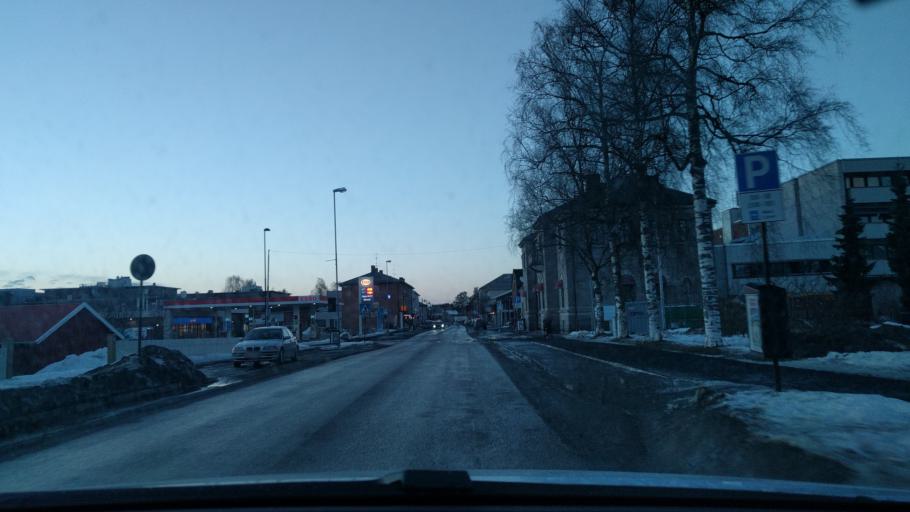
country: NO
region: Hedmark
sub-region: Elverum
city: Elverum
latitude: 60.8794
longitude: 11.5647
